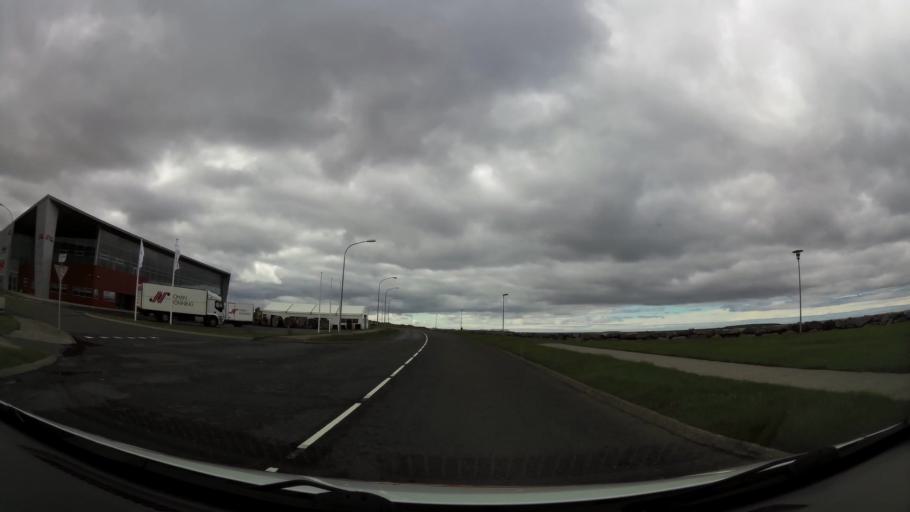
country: IS
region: Capital Region
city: Reykjavik
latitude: 64.1552
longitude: -21.8748
